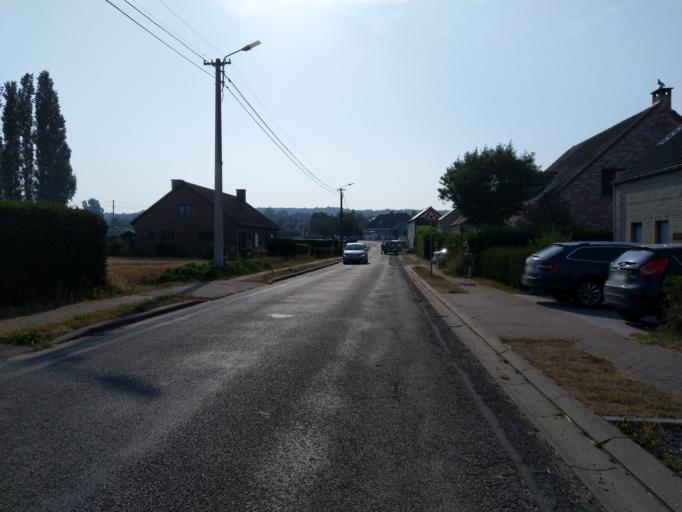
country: BE
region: Wallonia
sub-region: Province du Hainaut
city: Braine-le-Comte
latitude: 50.6103
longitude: 4.1583
